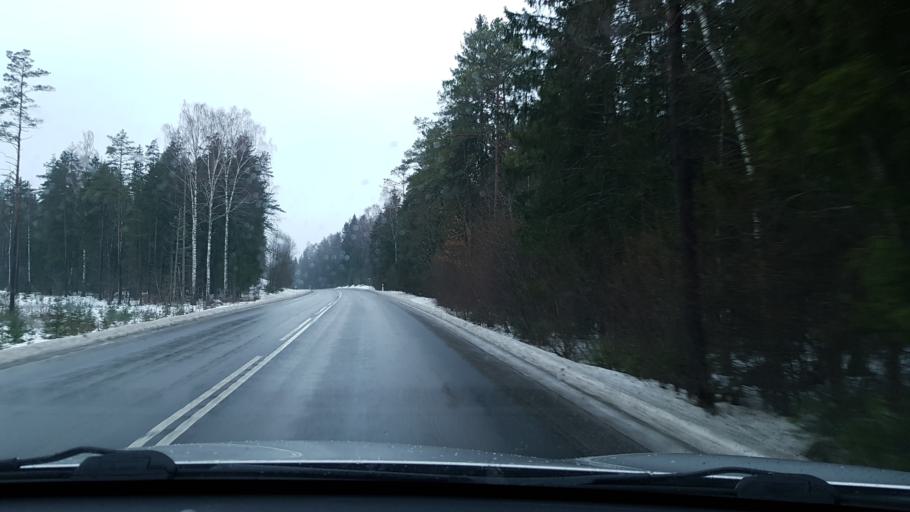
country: EE
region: Raplamaa
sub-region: Maerjamaa vald
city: Marjamaa
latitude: 58.9302
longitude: 24.3812
